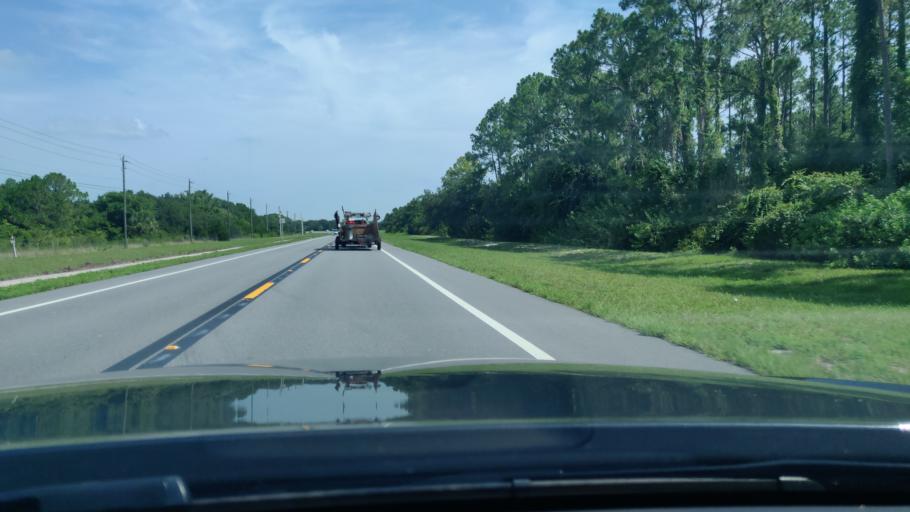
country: US
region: Florida
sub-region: Flagler County
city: Flagler Beach
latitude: 29.5123
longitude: -81.1627
